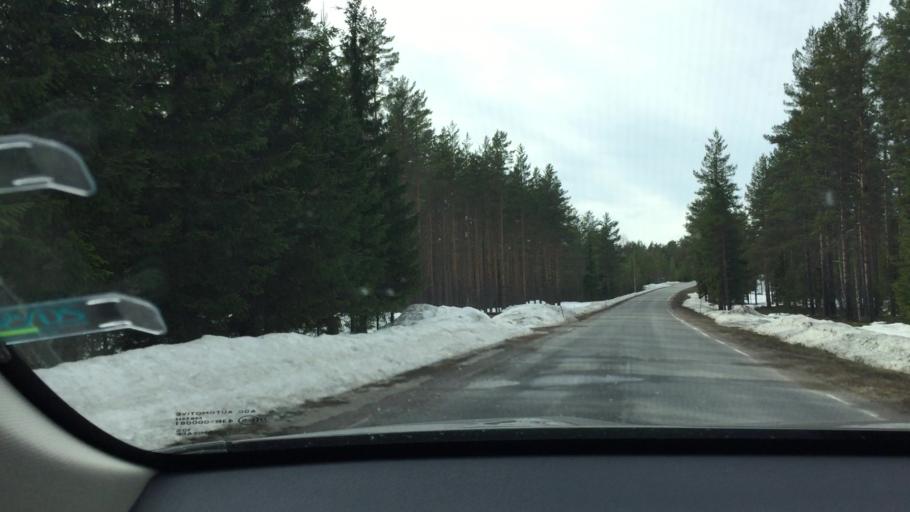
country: NO
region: Hedmark
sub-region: Trysil
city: Innbygda
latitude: 61.0640
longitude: 12.5977
